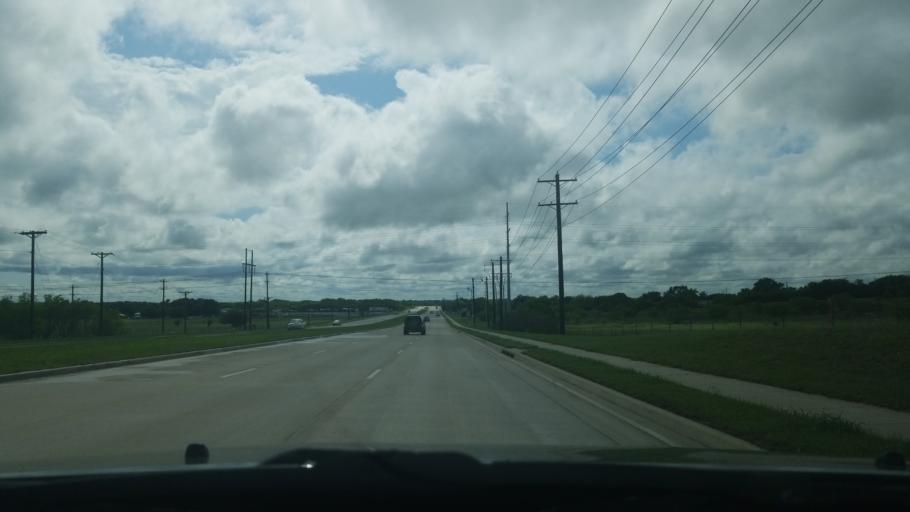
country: US
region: Texas
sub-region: Denton County
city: Krum
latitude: 33.2315
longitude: -97.2086
